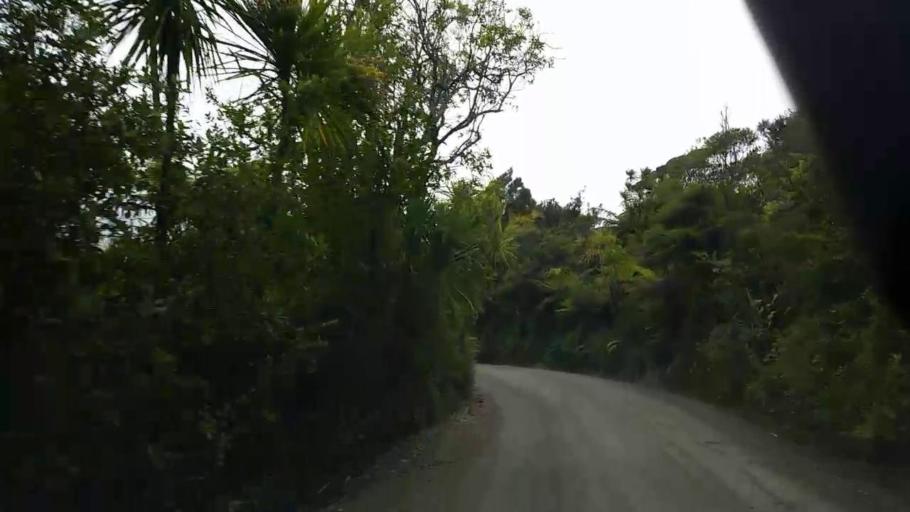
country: NZ
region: Auckland
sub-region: Auckland
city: Muriwai Beach
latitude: -36.9270
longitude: 174.4988
